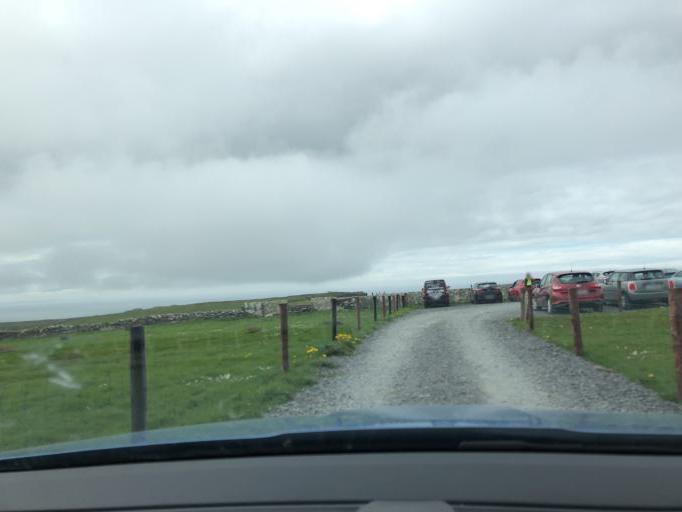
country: IE
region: Munster
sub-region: An Clar
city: Kilrush
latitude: 52.9639
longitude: -9.4342
